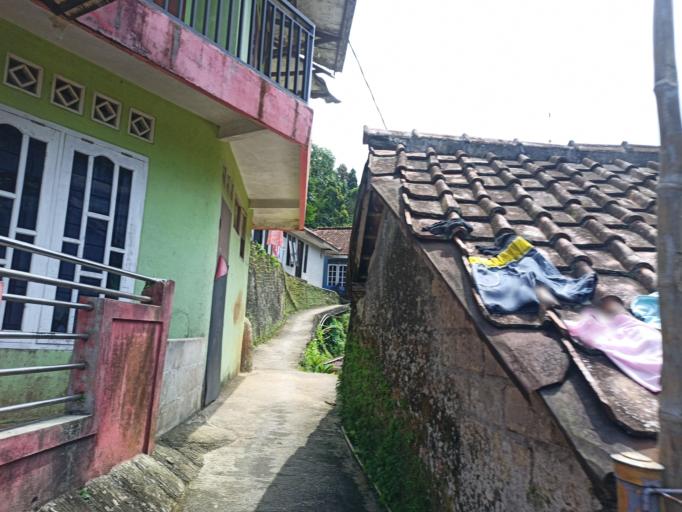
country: ID
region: West Java
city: Caringin
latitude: -6.6420
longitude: 106.9097
